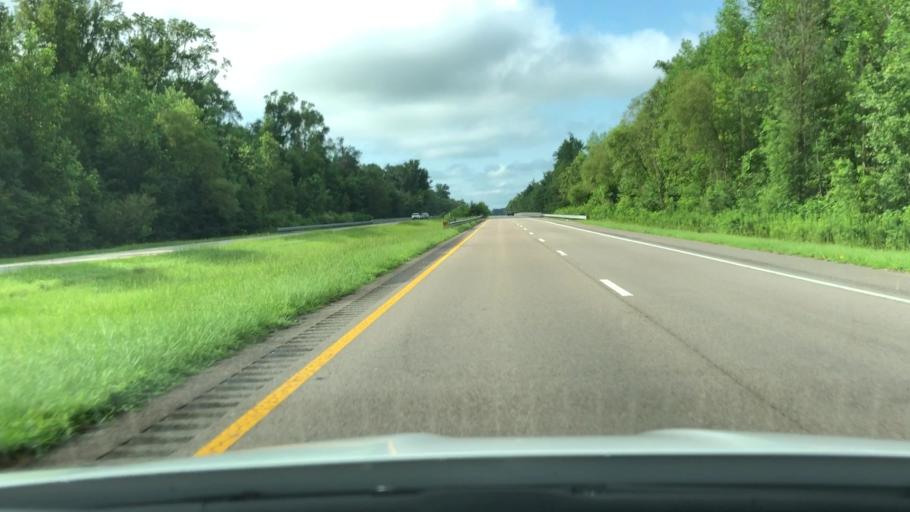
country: US
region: Virginia
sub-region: City of Portsmouth
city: Portsmouth Heights
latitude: 36.6353
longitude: -76.3632
